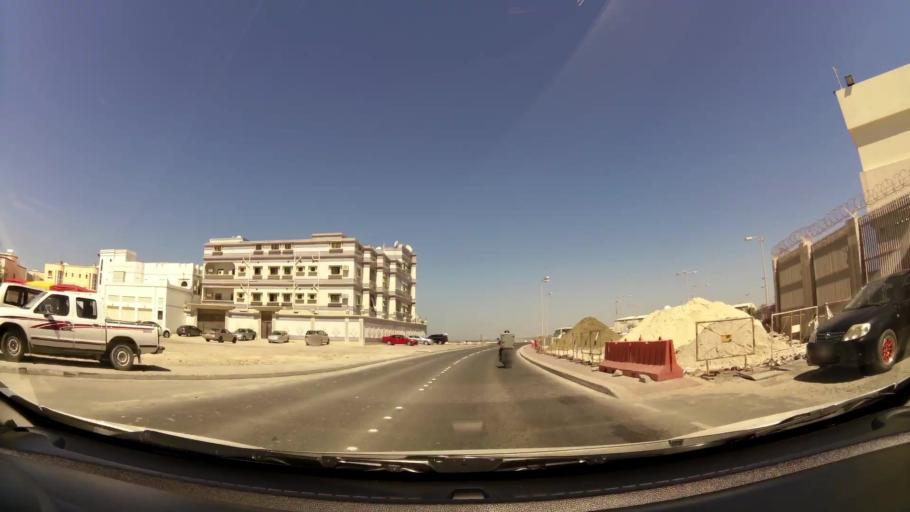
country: BH
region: Muharraq
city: Al Muharraq
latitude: 26.2771
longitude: 50.6124
